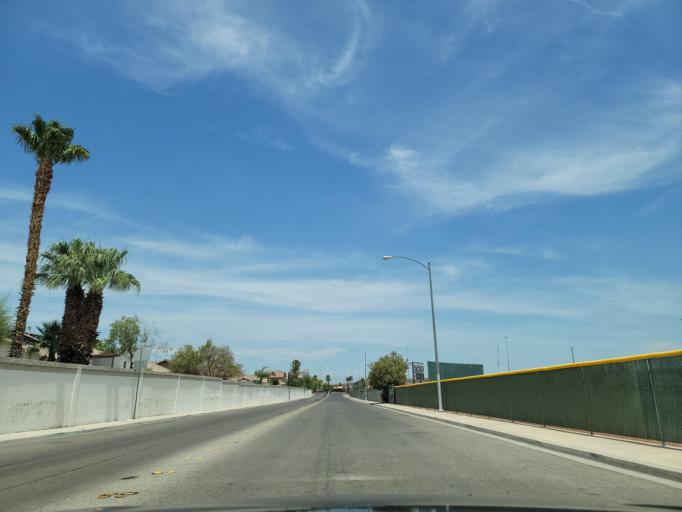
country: US
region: Nevada
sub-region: Clark County
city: Whitney
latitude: 36.0251
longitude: -115.1318
